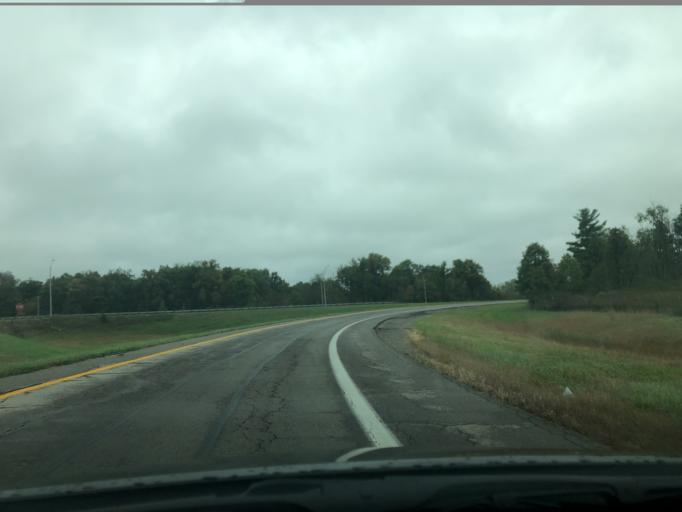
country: US
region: Ohio
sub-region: Champaign County
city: North Lewisburg
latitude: 40.3228
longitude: -83.5848
